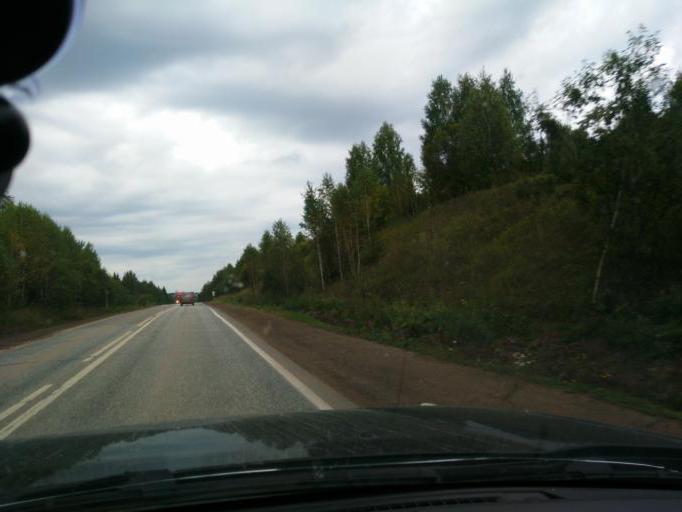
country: RU
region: Perm
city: Chernushka
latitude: 56.7993
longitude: 56.0717
